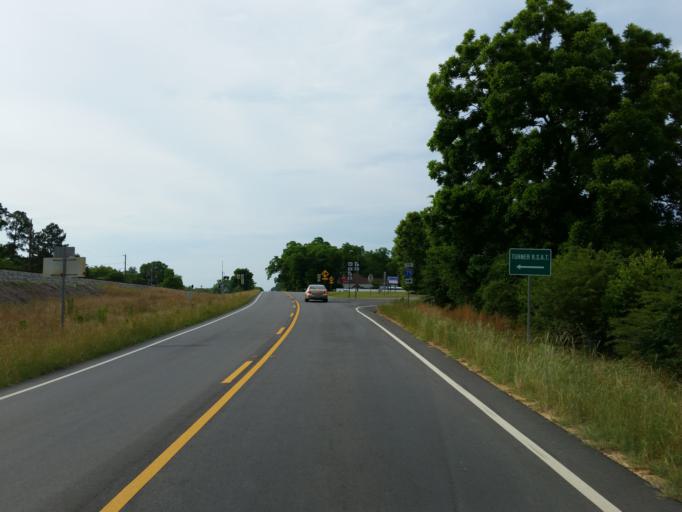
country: US
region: Georgia
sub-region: Turner County
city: Ashburn
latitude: 31.6647
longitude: -83.6327
